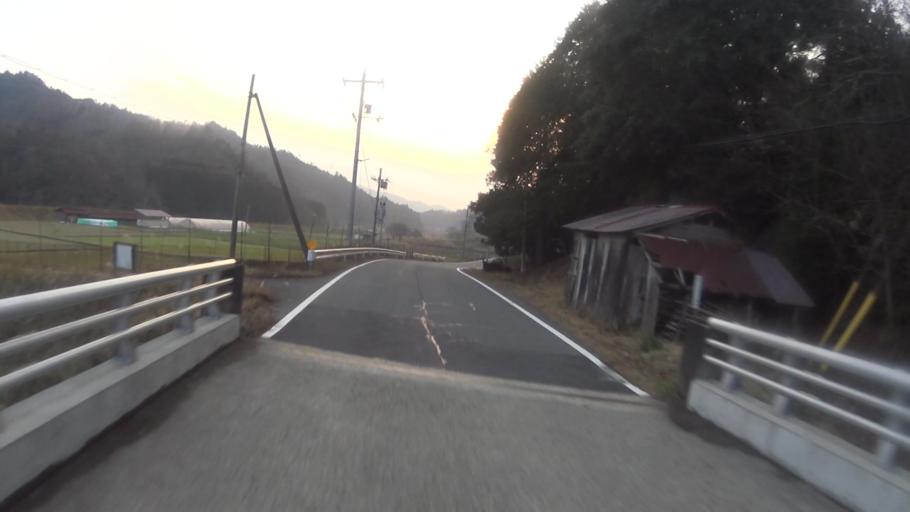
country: JP
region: Kyoto
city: Maizuru
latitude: 35.3838
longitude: 135.4549
